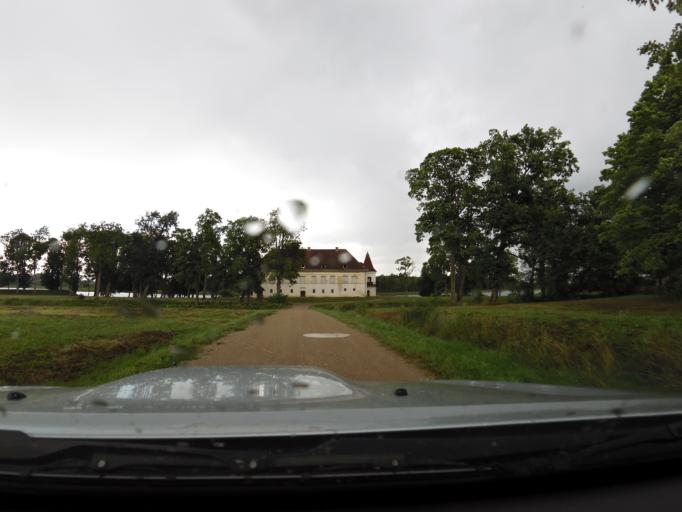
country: LT
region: Vilnius County
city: Ukmerge
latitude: 55.2853
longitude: 24.5133
